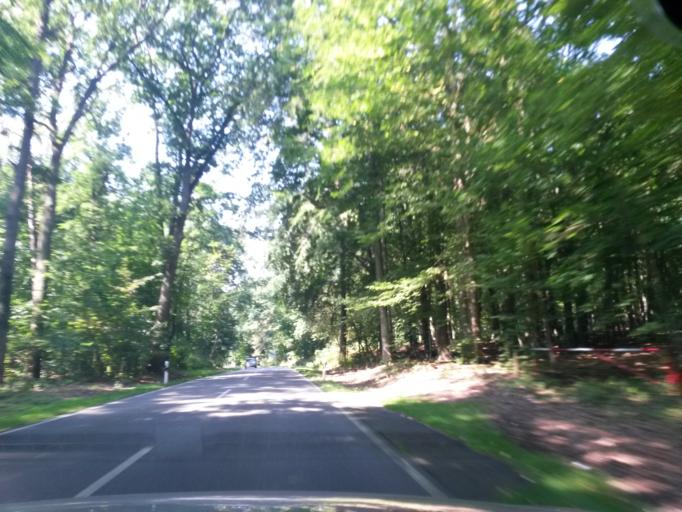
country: DE
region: Brandenburg
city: Marienwerder
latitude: 52.9111
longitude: 13.6524
